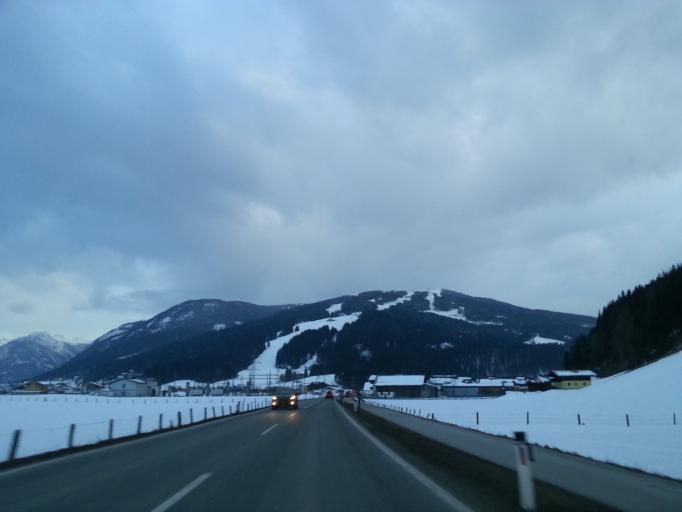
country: AT
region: Salzburg
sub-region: Politischer Bezirk Sankt Johann im Pongau
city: Flachau
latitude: 47.3676
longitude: 13.3858
